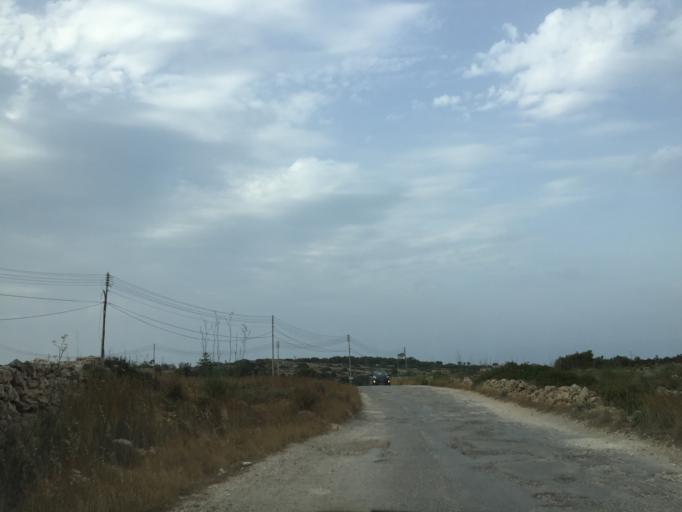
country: MT
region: L-Imgarr
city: Imgarr
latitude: 35.9317
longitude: 14.3866
